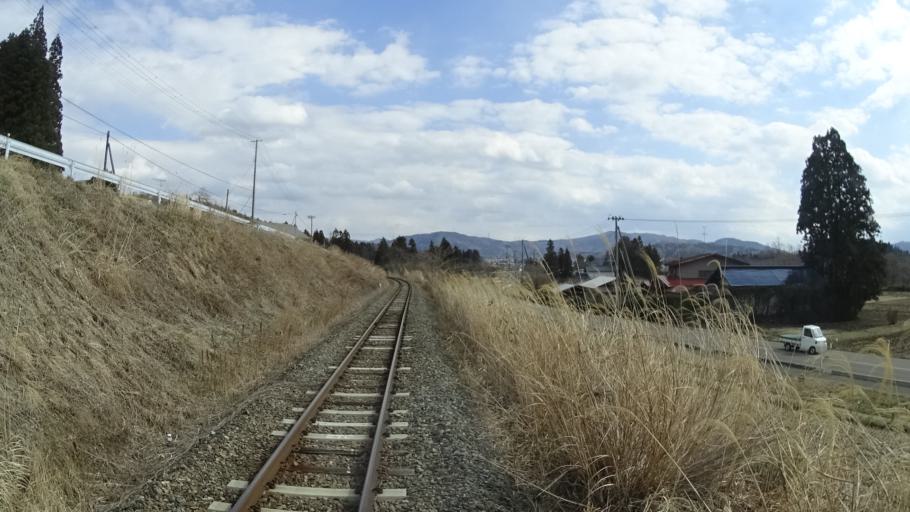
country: JP
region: Iwate
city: Hanamaki
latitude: 39.3767
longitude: 141.2501
